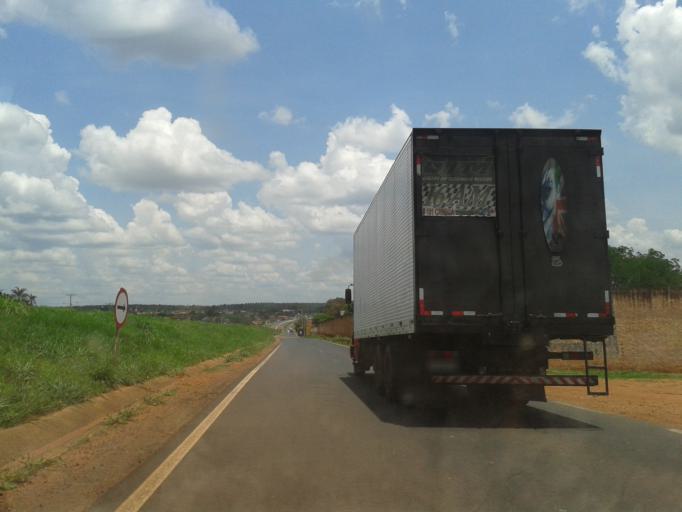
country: BR
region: Minas Gerais
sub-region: Monte Alegre De Minas
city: Monte Alegre de Minas
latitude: -18.8663
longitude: -48.8677
